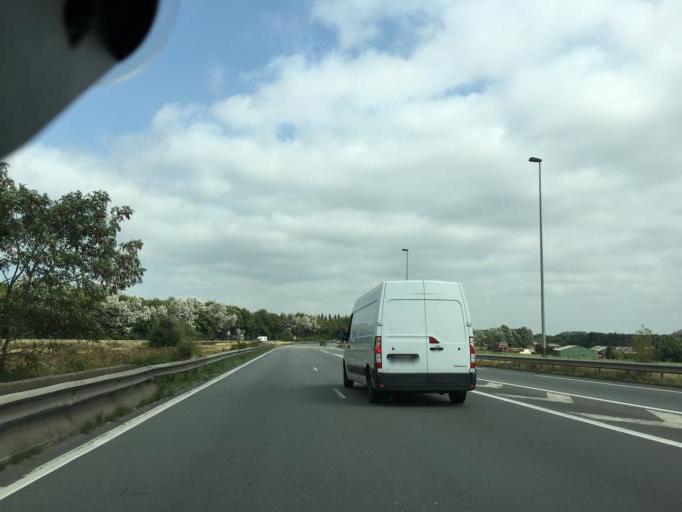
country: FR
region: Nord-Pas-de-Calais
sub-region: Departement du Pas-de-Calais
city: Noyelles-Godault
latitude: 50.4258
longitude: 2.9876
